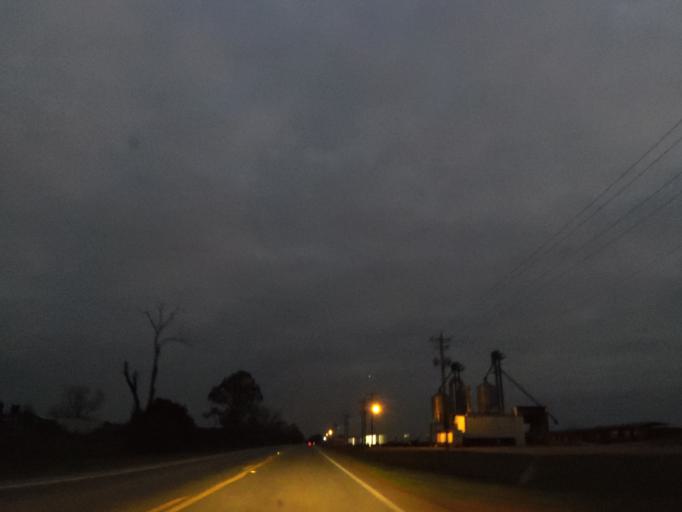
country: US
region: Georgia
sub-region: Colquitt County
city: Moultrie
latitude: 31.2957
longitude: -83.8932
